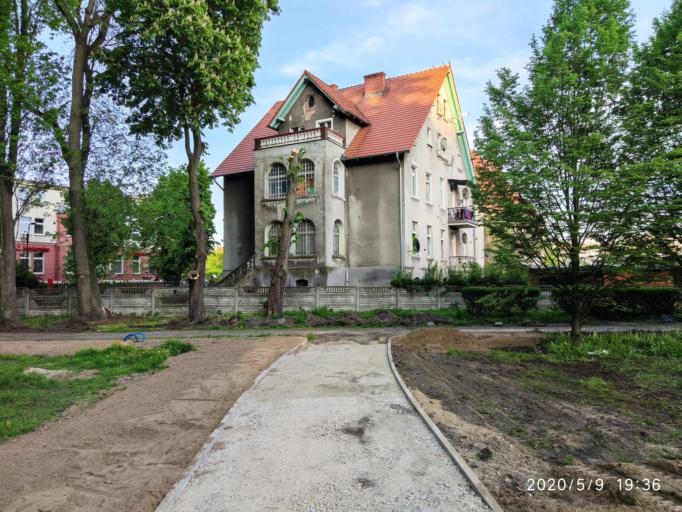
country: PL
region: Lubusz
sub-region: Powiat zielonogorski
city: Sulechow
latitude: 52.0865
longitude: 15.6211
